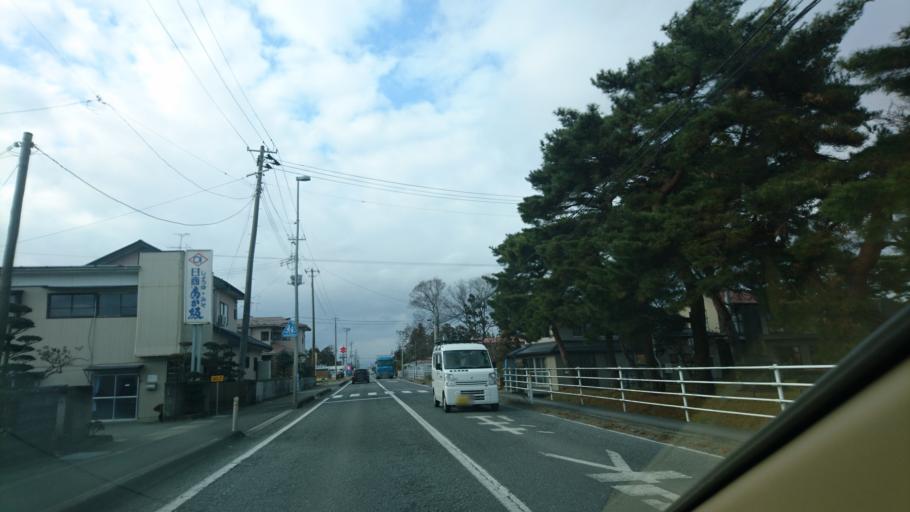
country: JP
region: Miyagi
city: Kogota
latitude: 38.5623
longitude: 141.0181
